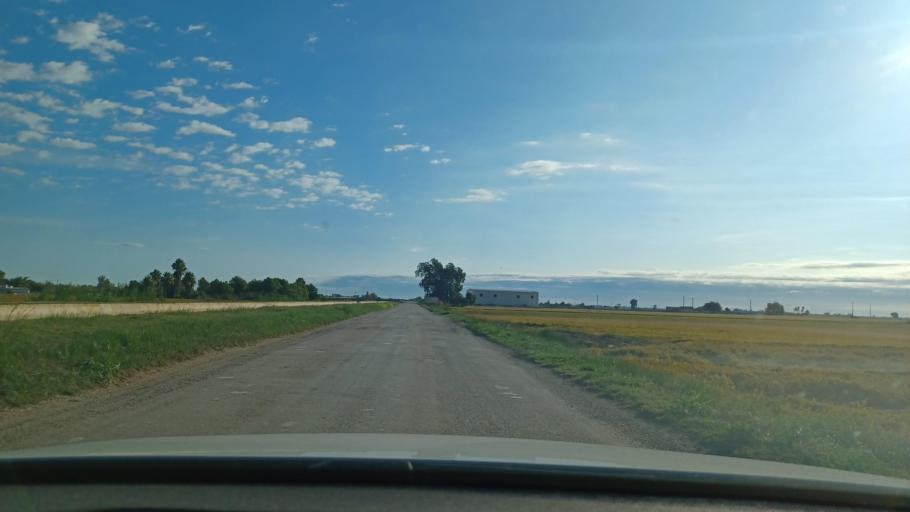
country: ES
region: Catalonia
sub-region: Provincia de Tarragona
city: Amposta
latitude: 40.7011
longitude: 0.6221
